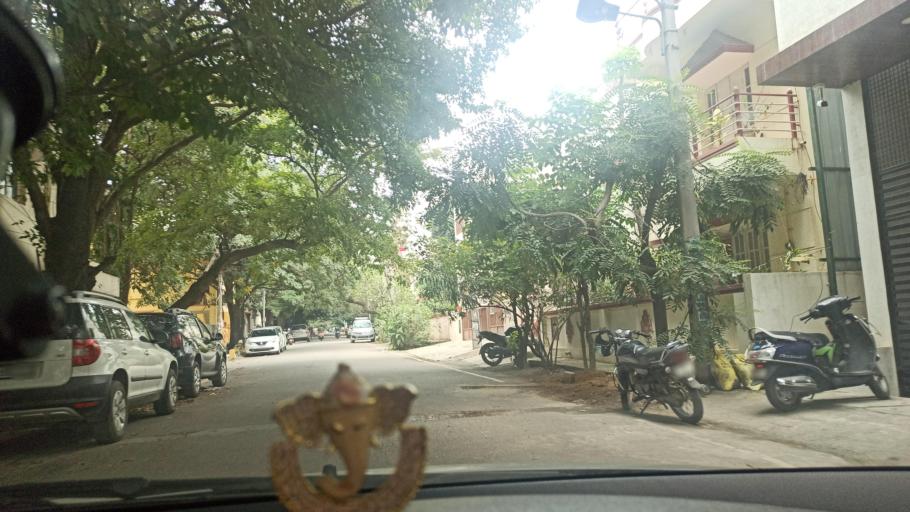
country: IN
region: Karnataka
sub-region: Bangalore Urban
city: Bangalore
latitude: 12.9157
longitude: 77.6472
